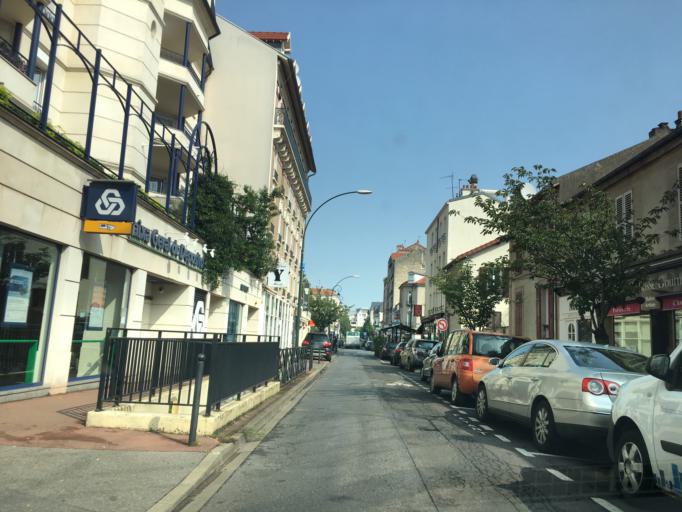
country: FR
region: Ile-de-France
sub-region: Departement du Val-de-Marne
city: Saint-Maur-des-Fosses
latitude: 48.8017
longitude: 2.4860
